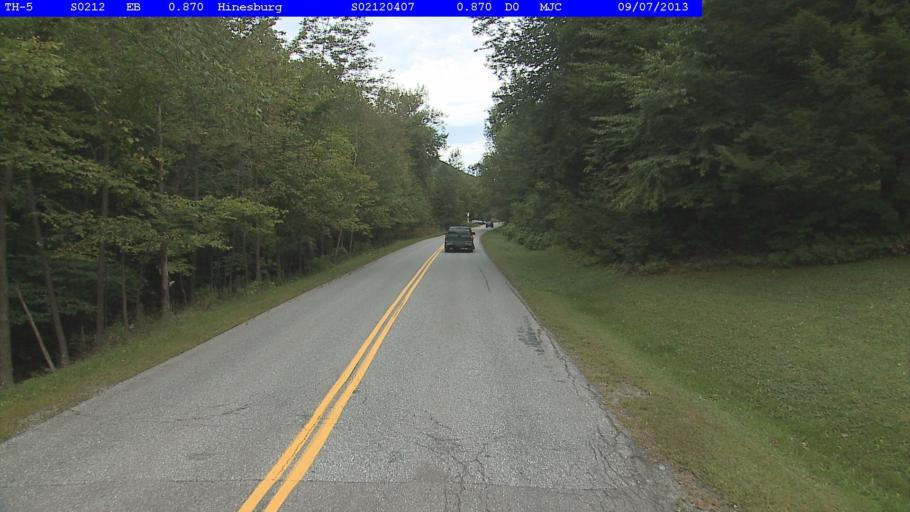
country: US
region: Vermont
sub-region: Chittenden County
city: Hinesburg
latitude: 44.2931
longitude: -73.0533
